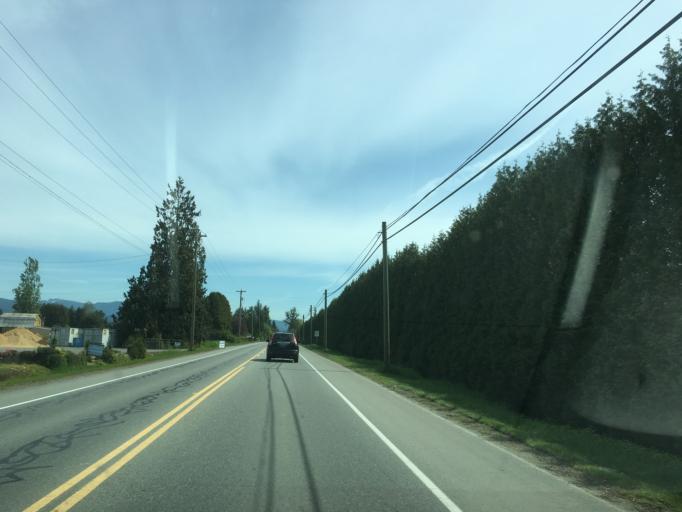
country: CA
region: British Columbia
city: Pitt Meadows
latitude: 49.2443
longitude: -122.7079
